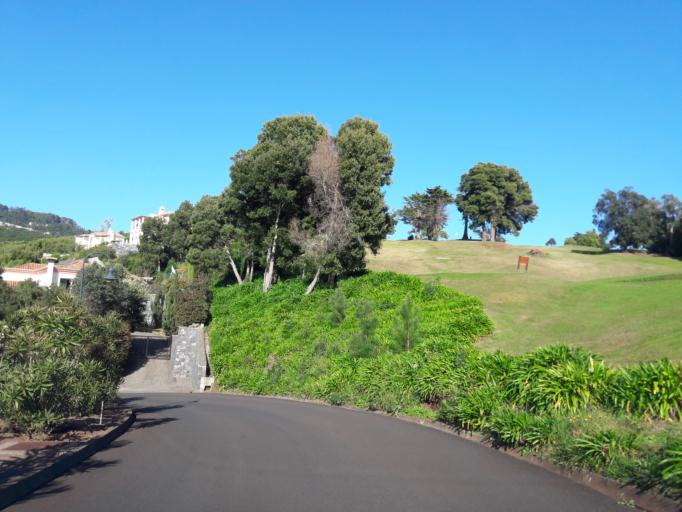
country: PT
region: Madeira
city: Canico
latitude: 32.6540
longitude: -16.8720
